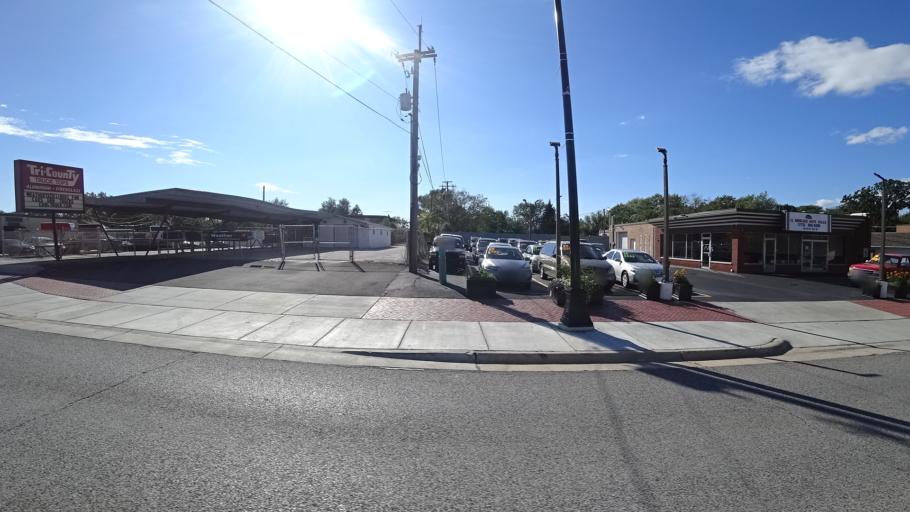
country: US
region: Illinois
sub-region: Cook County
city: Oak Forest
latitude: 41.6130
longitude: -87.7369
